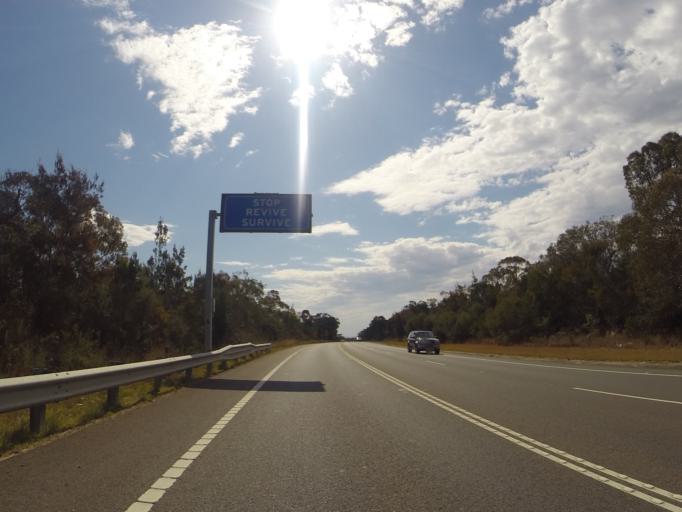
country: AU
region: New South Wales
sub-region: Liverpool
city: Holsworthy
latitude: -34.0415
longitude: 150.9592
